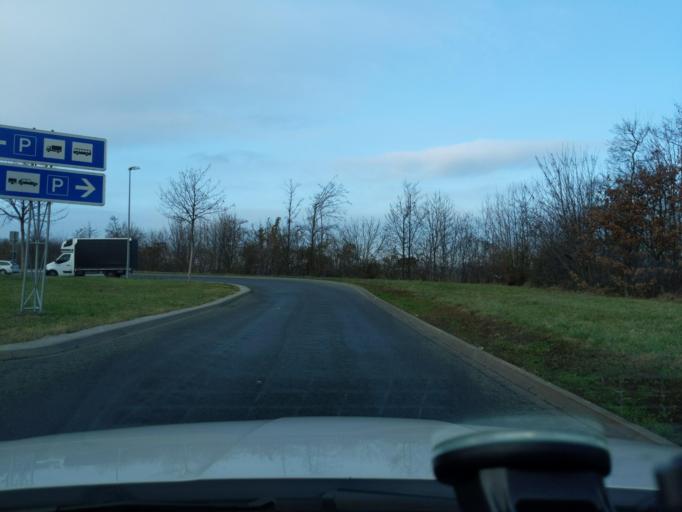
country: DE
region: North Rhine-Westphalia
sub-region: Regierungsbezirk Arnsberg
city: Welver
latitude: 51.5421
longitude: 8.0202
